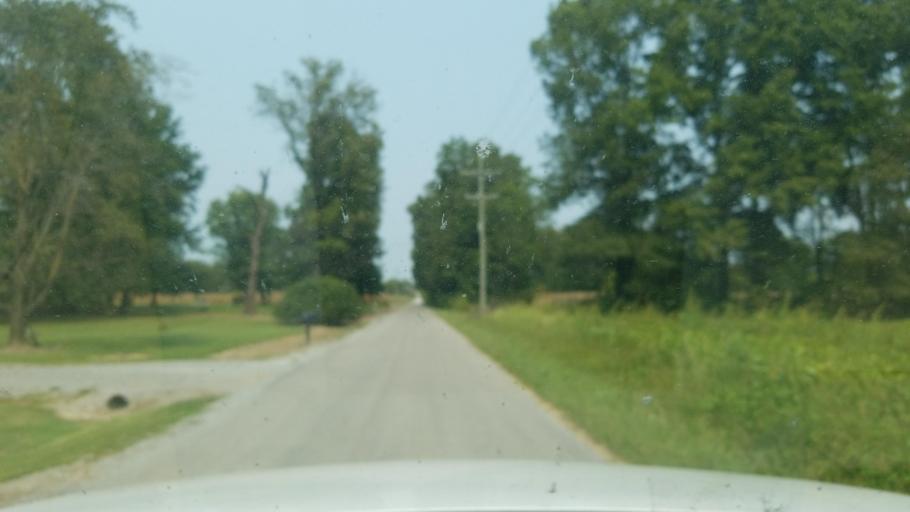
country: US
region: Illinois
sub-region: Saline County
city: Harrisburg
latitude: 37.8081
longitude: -88.5167
